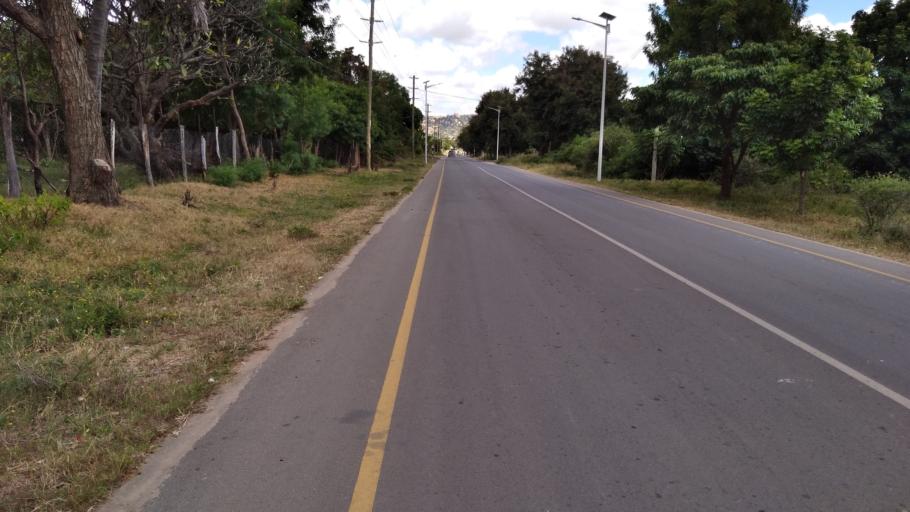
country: TZ
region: Dodoma
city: Dodoma
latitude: -6.1881
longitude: 35.7503
